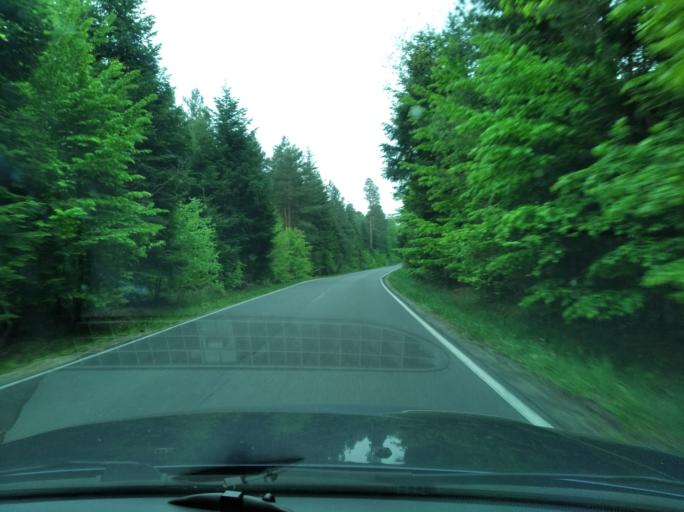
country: PL
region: Subcarpathian Voivodeship
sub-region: Powiat kolbuszowski
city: Kolbuszowa
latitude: 50.1694
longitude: 21.7598
